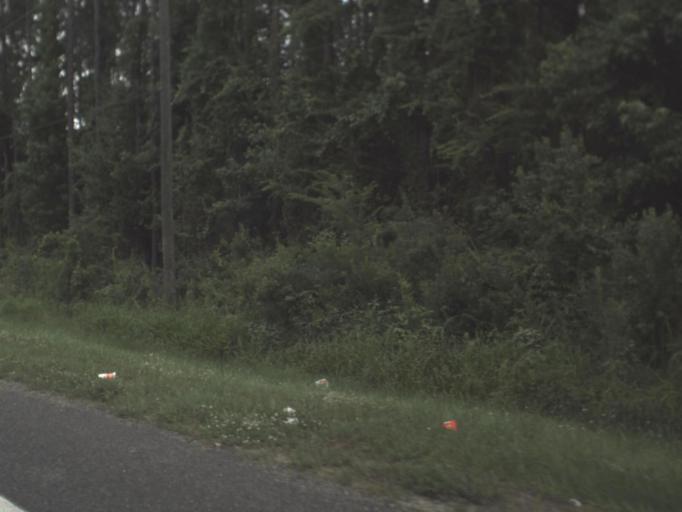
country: US
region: Florida
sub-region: Nassau County
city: Callahan
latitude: 30.6086
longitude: -81.8378
